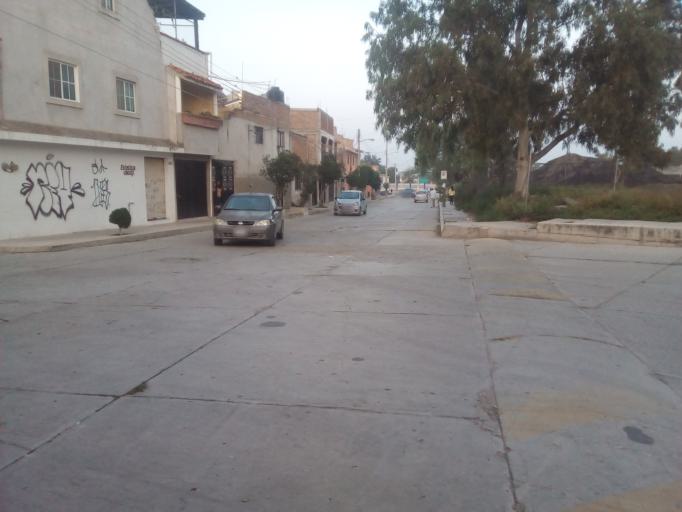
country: MX
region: Guerrero
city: San Luis de la Paz
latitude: 21.2903
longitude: -100.5251
